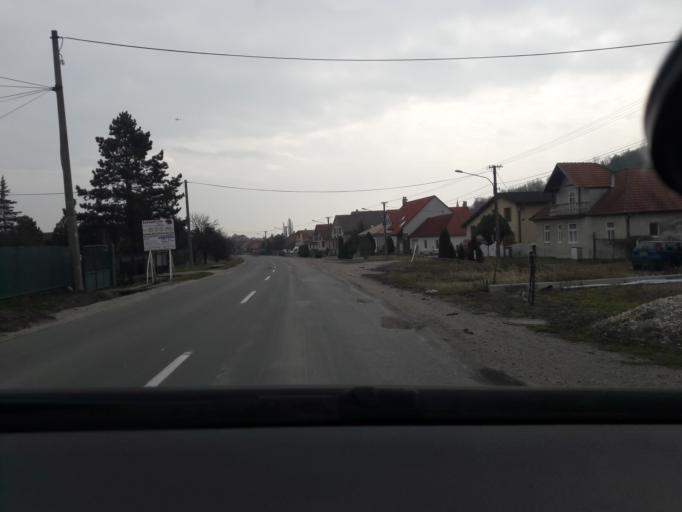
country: SK
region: Trnavsky
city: Smolenice
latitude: 48.4727
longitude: 17.4344
